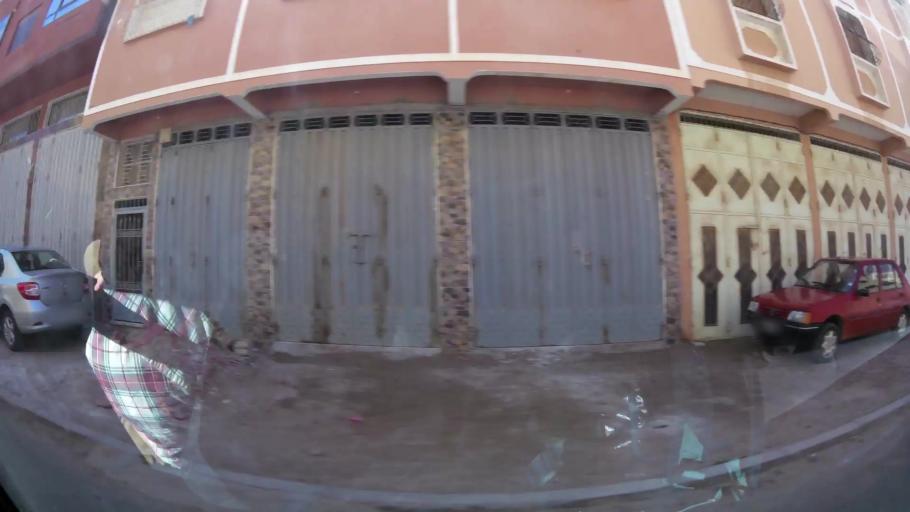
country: MA
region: Souss-Massa-Draa
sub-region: Inezgane-Ait Mellou
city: Inezgane
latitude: 30.3227
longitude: -9.5003
